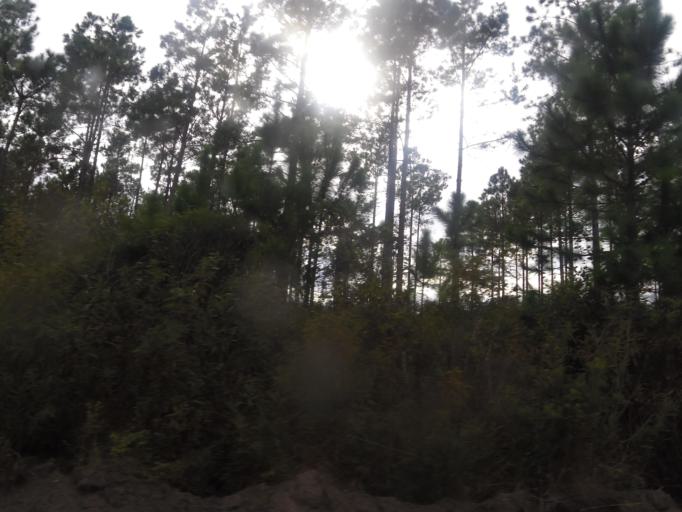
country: US
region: Florida
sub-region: Flagler County
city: Bunnell
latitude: 29.5617
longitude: -81.3335
